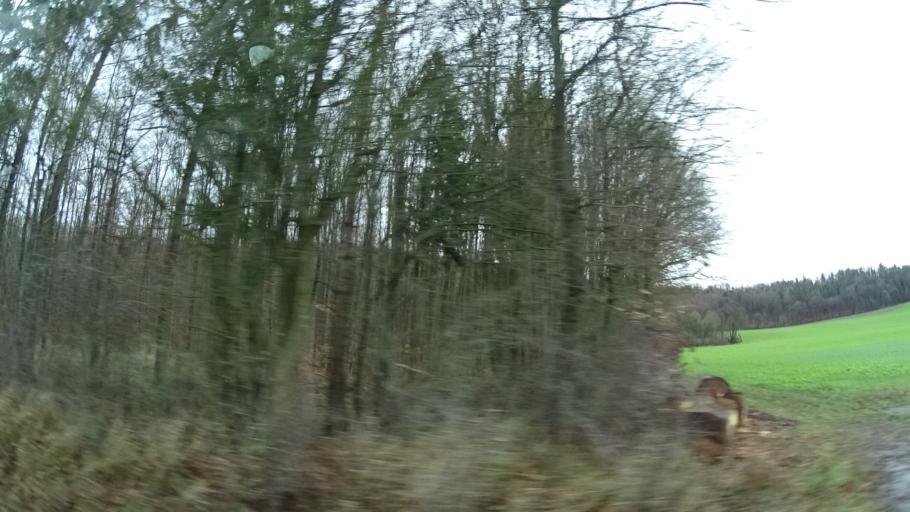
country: DE
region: Bavaria
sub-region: Regierungsbezirk Unterfranken
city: Willmars
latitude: 50.5448
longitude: 10.2360
